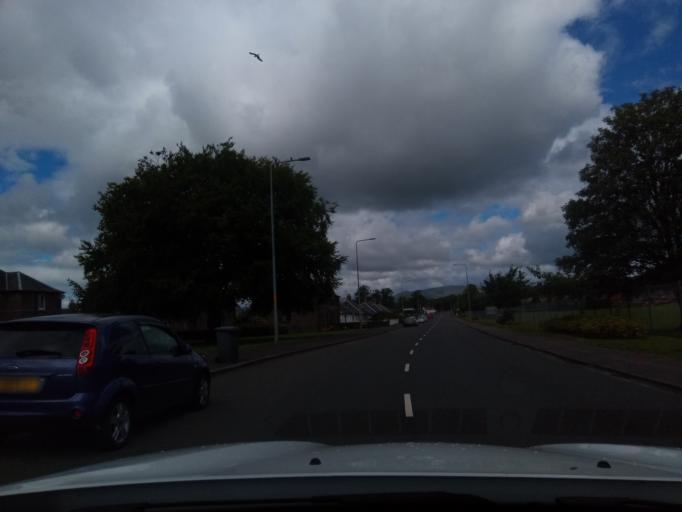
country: GB
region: Scotland
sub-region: Fife
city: Kincardine
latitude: 56.0702
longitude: -3.7189
